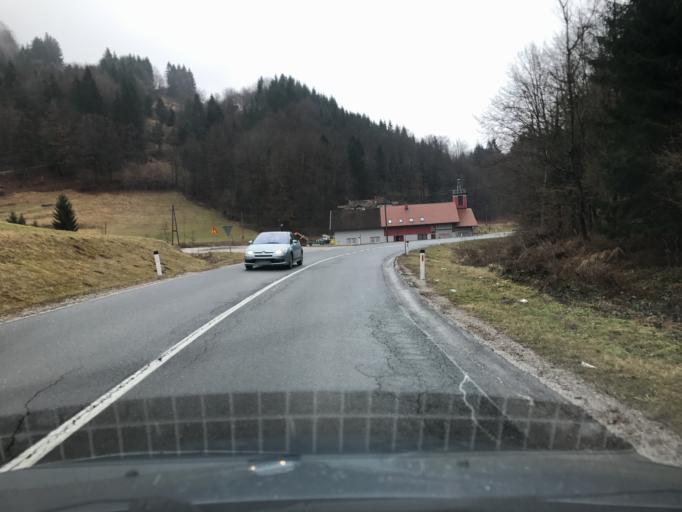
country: SI
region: Gornji Grad
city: Gornji Grad
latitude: 46.2164
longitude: 14.8432
